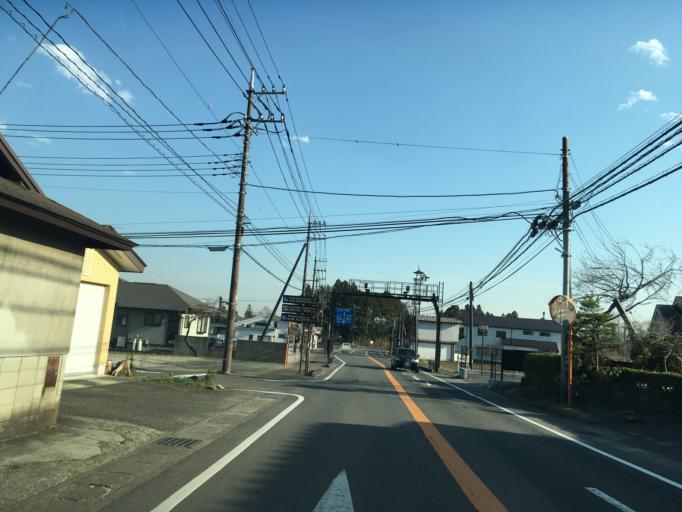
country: JP
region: Tochigi
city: Kuroiso
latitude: 37.0445
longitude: 140.0133
